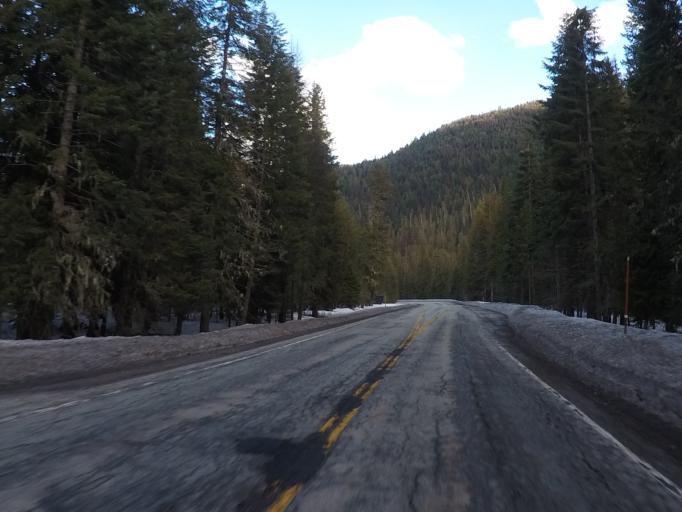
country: US
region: Montana
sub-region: Ravalli County
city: Hamilton
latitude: 46.5096
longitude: -114.7795
